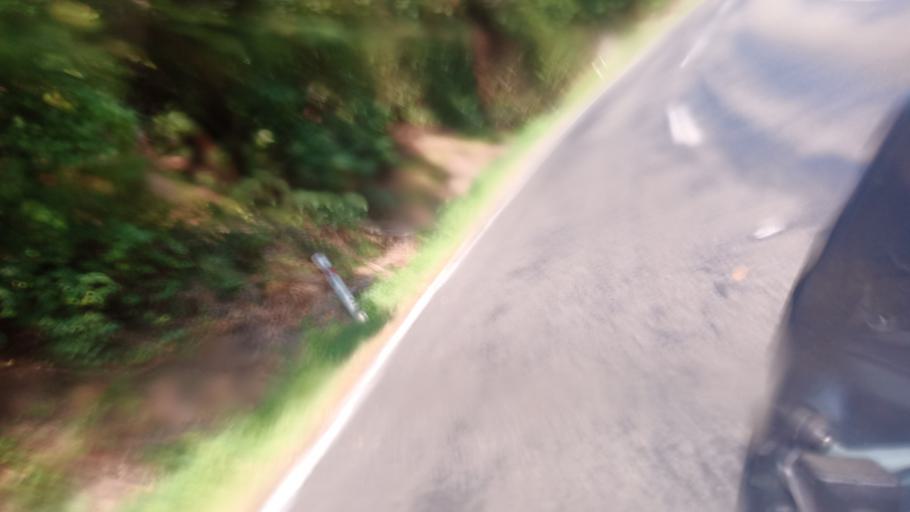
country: NZ
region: Bay of Plenty
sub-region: Opotiki District
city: Opotiki
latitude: -37.5991
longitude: 178.2966
